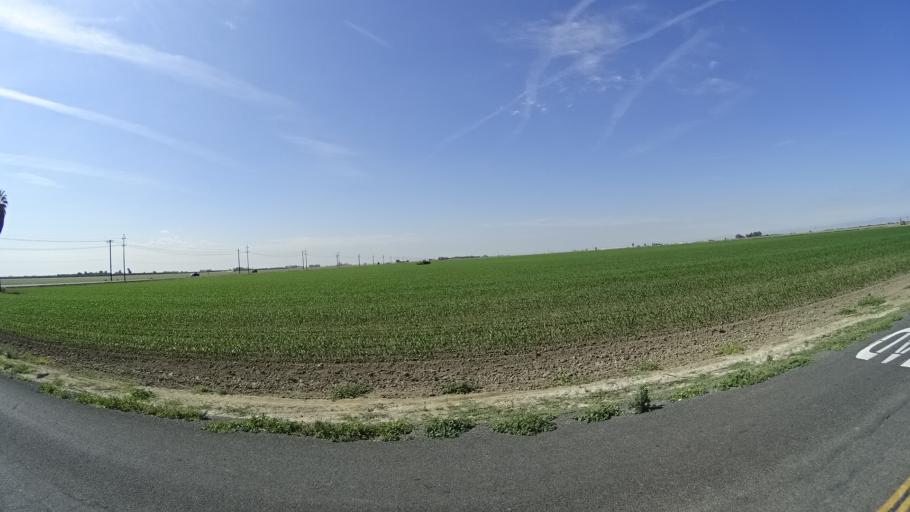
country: US
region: California
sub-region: Kings County
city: Home Garden
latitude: 36.2548
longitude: -119.6560
